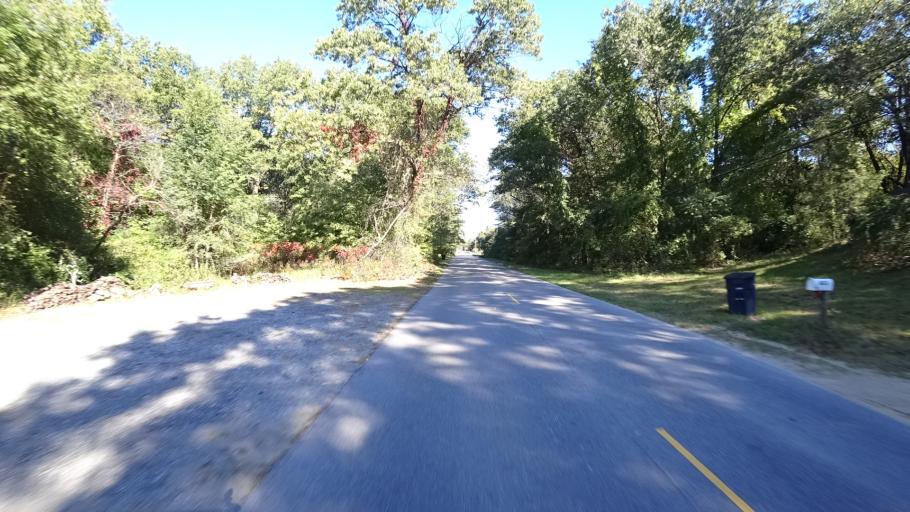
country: US
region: Indiana
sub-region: LaPorte County
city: Michigan City
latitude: 41.6929
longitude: -86.9324
